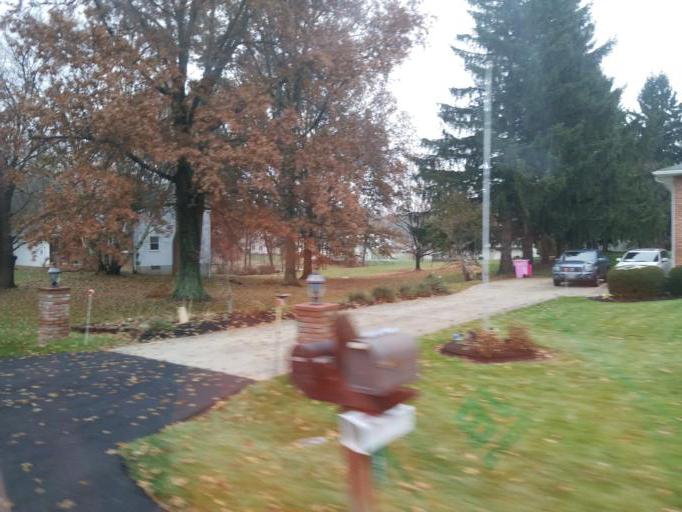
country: US
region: Ohio
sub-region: Richland County
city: Lexington
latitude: 40.6989
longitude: -82.5271
